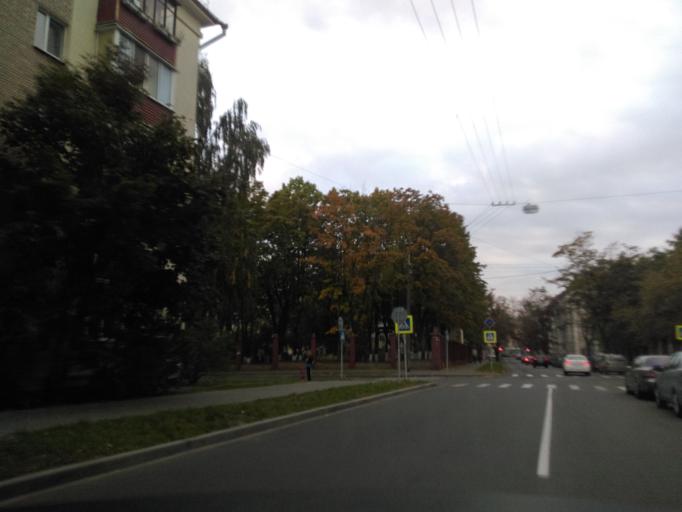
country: BY
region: Minsk
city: Minsk
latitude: 53.9111
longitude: 27.5833
